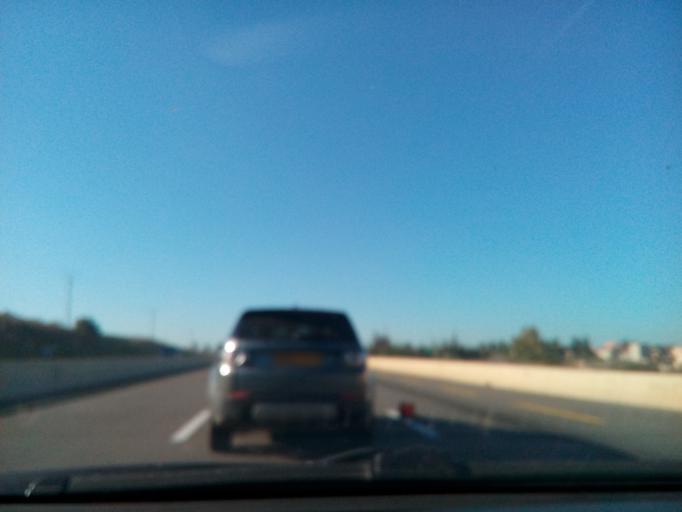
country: DZ
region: Chlef
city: Boukadir
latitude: 36.0563
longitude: 1.1417
